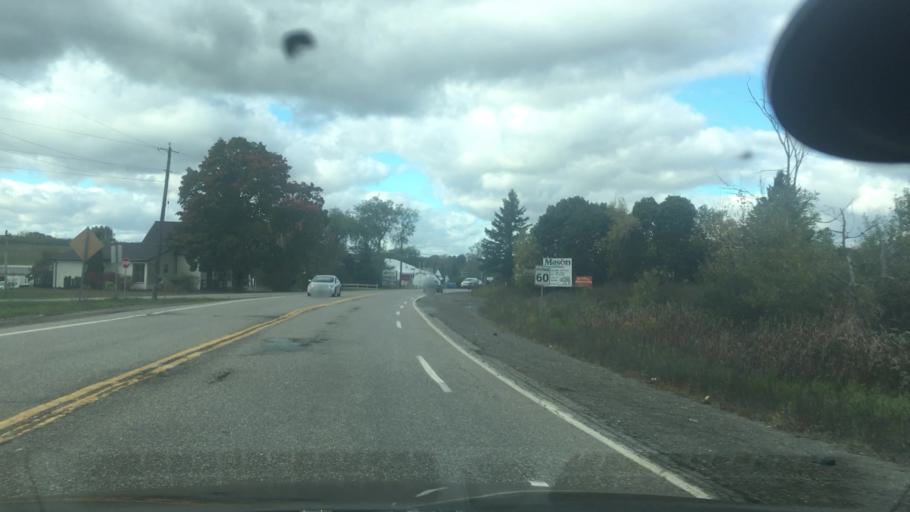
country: CA
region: Nova Scotia
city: Windsor
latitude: 44.9735
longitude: -64.1014
